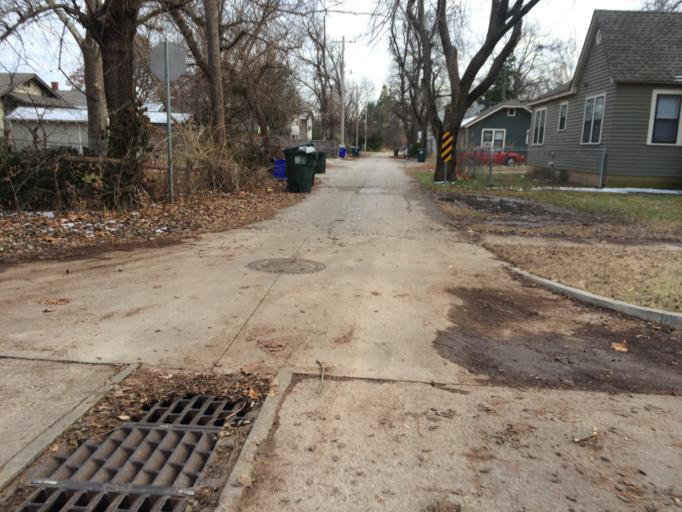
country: US
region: Oklahoma
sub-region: Cleveland County
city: Norman
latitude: 35.2142
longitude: -97.4379
